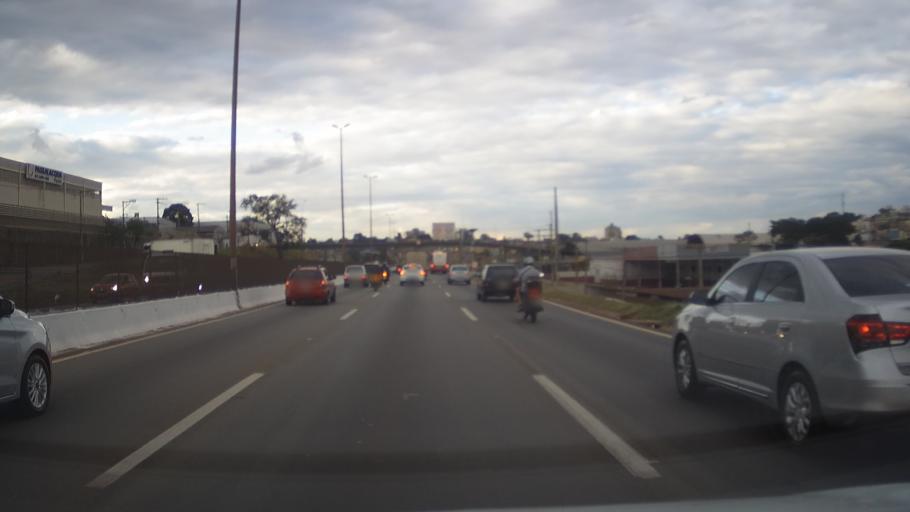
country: BR
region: Minas Gerais
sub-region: Contagem
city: Contagem
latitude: -19.9378
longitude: -44.0076
